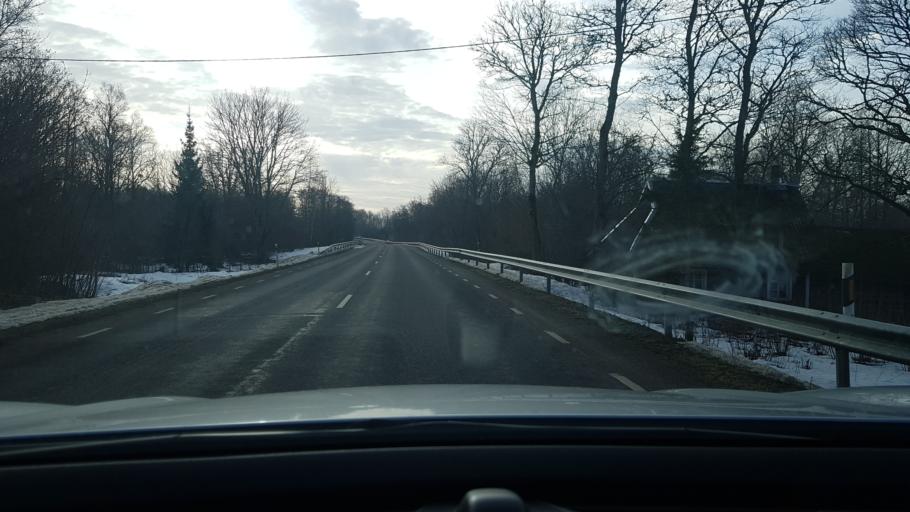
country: EE
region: Saare
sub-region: Kuressaare linn
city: Kuressaare
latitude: 58.3027
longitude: 22.5392
